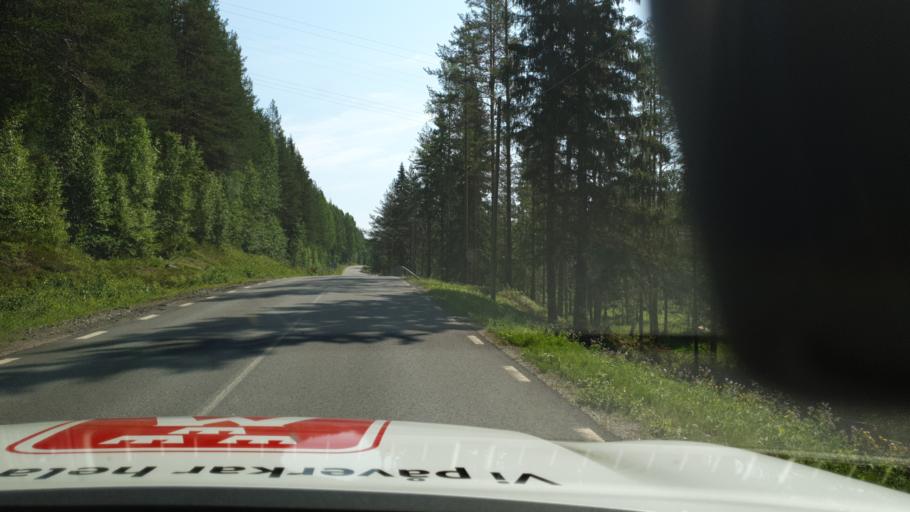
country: SE
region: Vaesterbotten
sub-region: Skelleftea Kommun
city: Langsele
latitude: 64.9451
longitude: 20.0305
